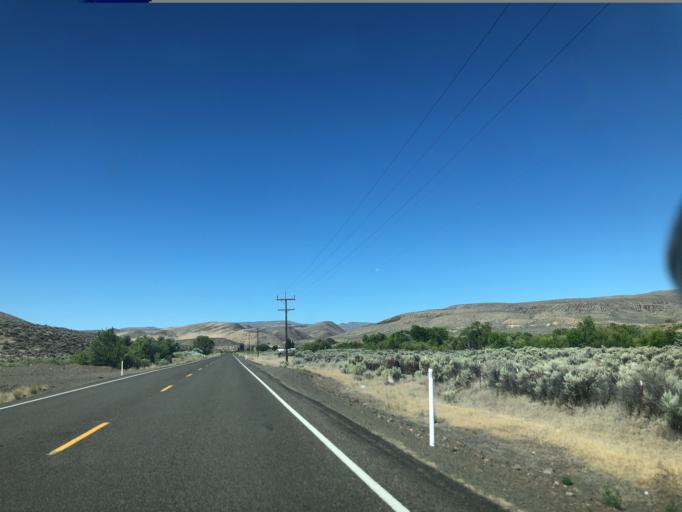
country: US
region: Oregon
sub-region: Malheur County
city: Vale
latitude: 43.8036
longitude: -117.6723
